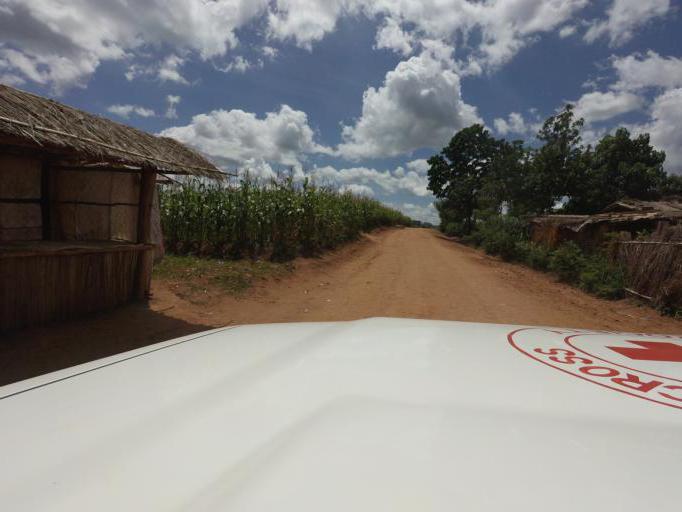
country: MW
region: Southern Region
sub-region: Thyolo District
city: Thyolo
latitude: -16.0295
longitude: 35.0476
